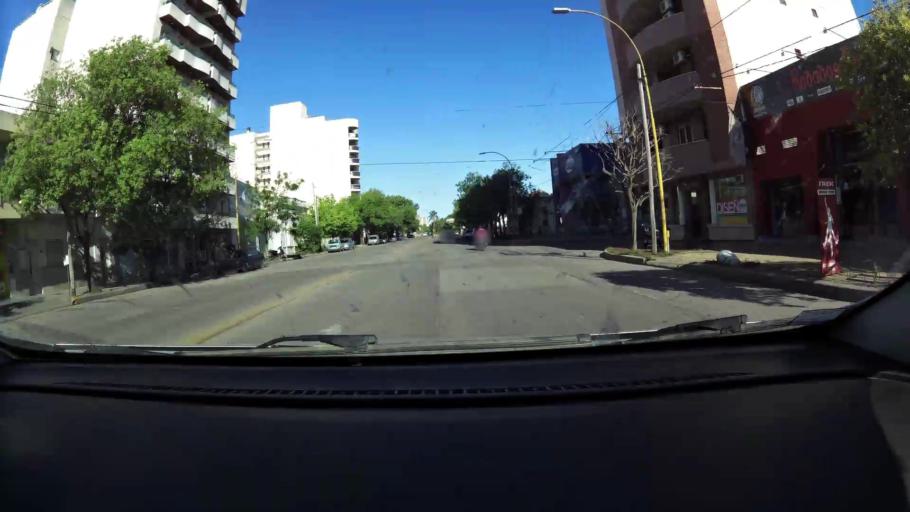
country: AR
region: Cordoba
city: San Francisco
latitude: -31.4294
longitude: -62.0943
